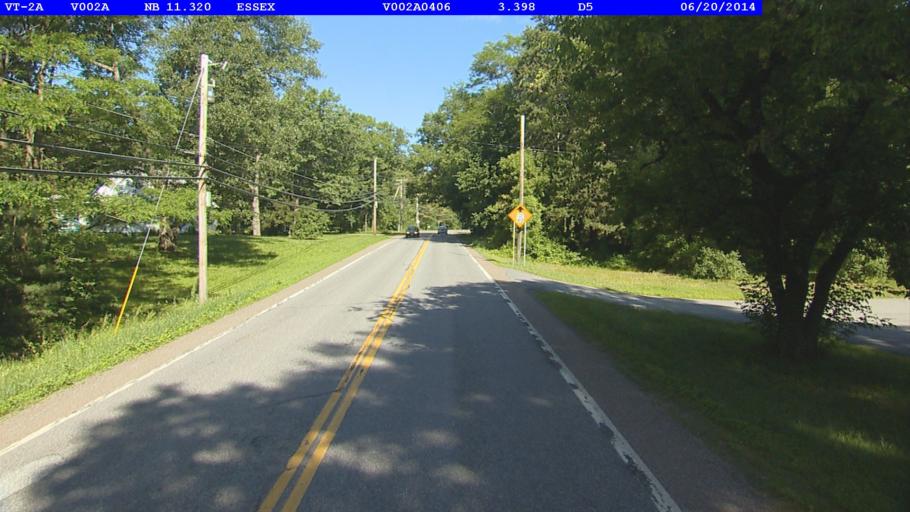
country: US
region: Vermont
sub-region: Chittenden County
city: Colchester
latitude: 44.5277
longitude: -73.1273
